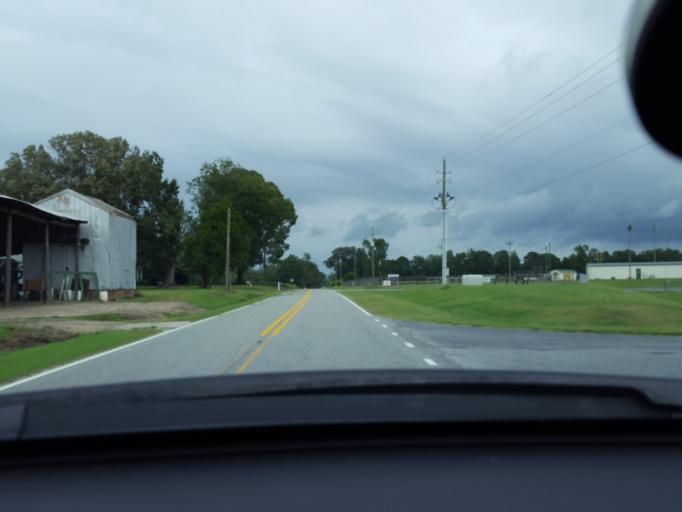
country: US
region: North Carolina
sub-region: Pitt County
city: Ayden
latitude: 35.4315
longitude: -77.4321
